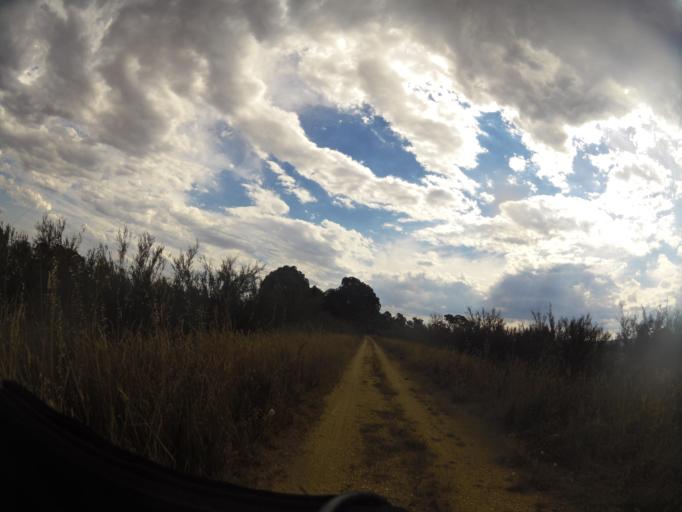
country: AU
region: Victoria
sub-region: Wellington
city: Heyfield
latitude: -38.0369
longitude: 146.6525
